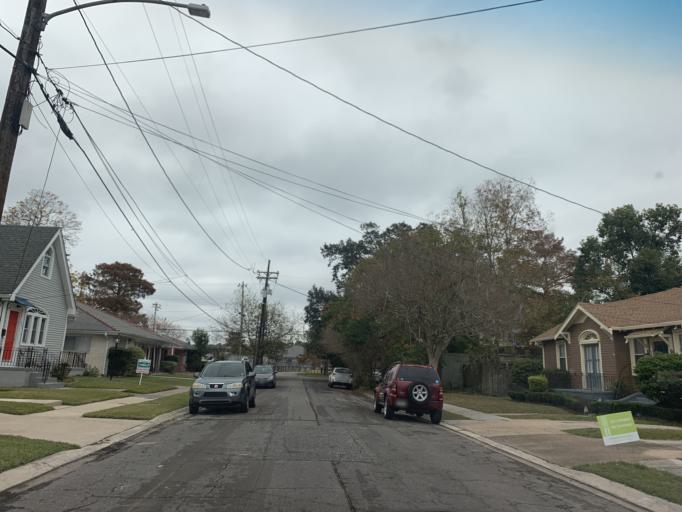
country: US
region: Louisiana
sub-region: Jefferson Parish
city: Metairie
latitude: 29.9880
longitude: -90.1079
